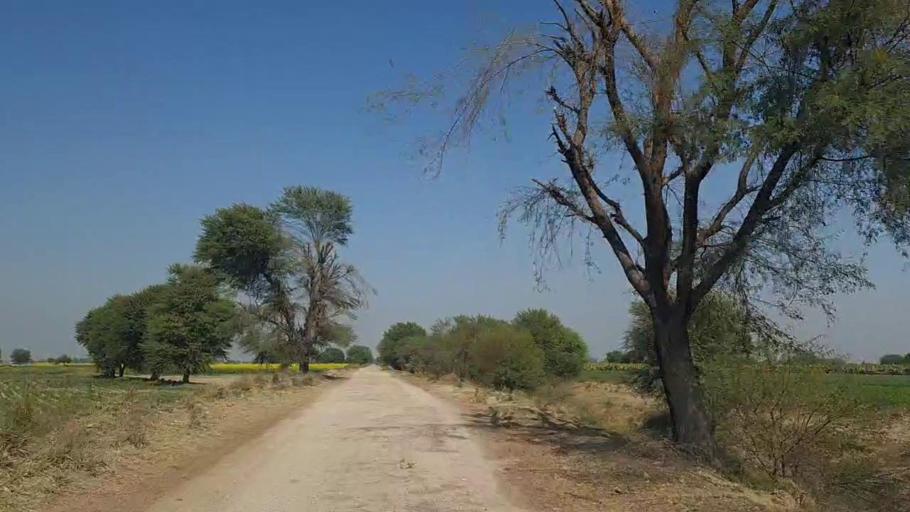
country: PK
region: Sindh
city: Shahpur Chakar
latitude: 26.1816
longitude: 68.5999
